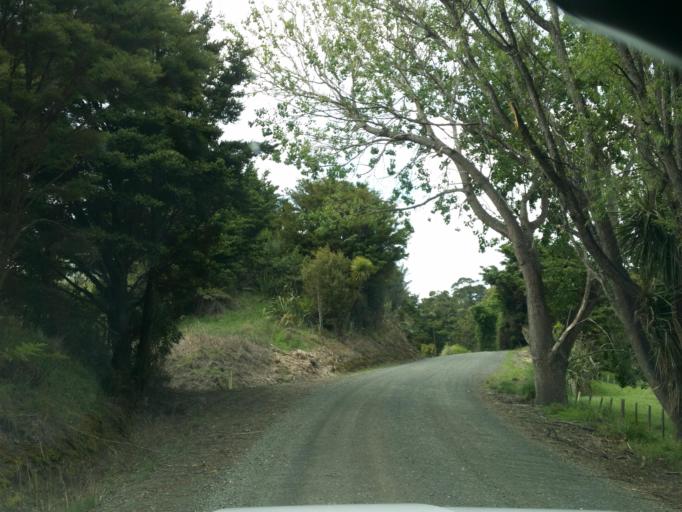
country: NZ
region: Northland
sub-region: Whangarei
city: Maungatapere
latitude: -35.9014
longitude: 174.1471
